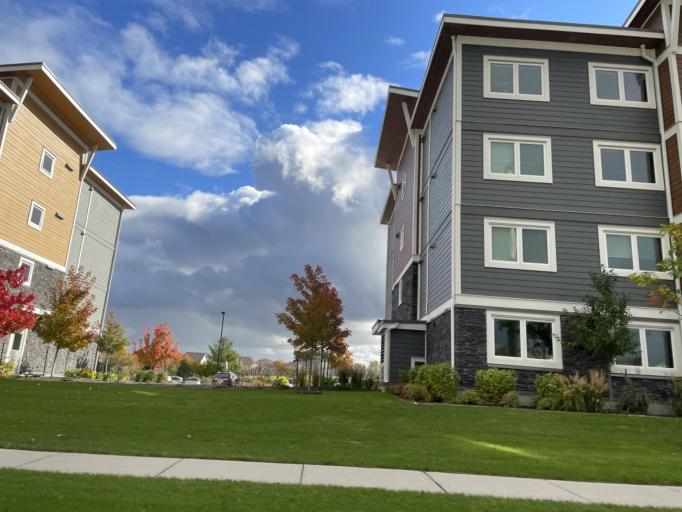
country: CA
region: Ontario
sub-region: Wellington County
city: Guelph
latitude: 43.5284
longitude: -80.2809
